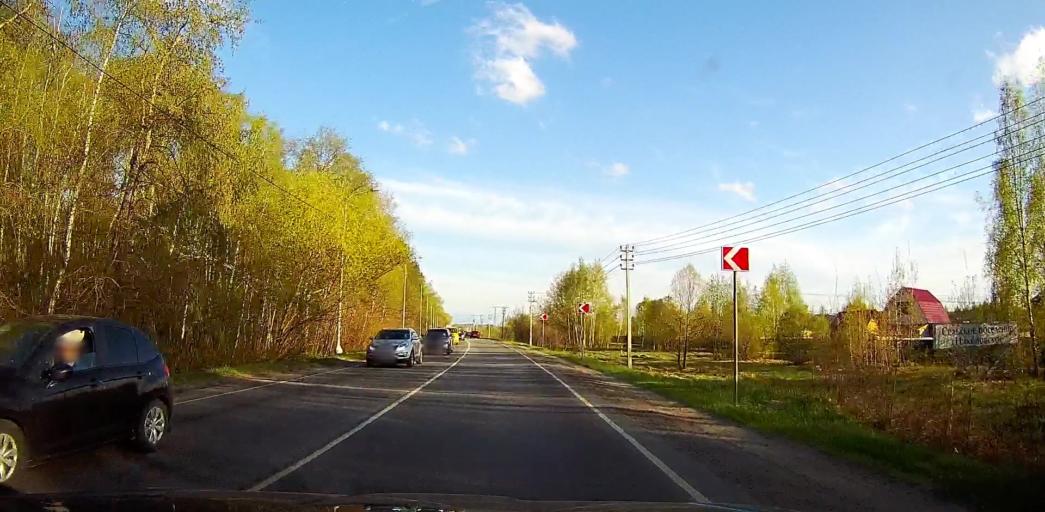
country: RU
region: Moskovskaya
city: Bronnitsy
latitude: 55.3808
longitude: 38.2083
